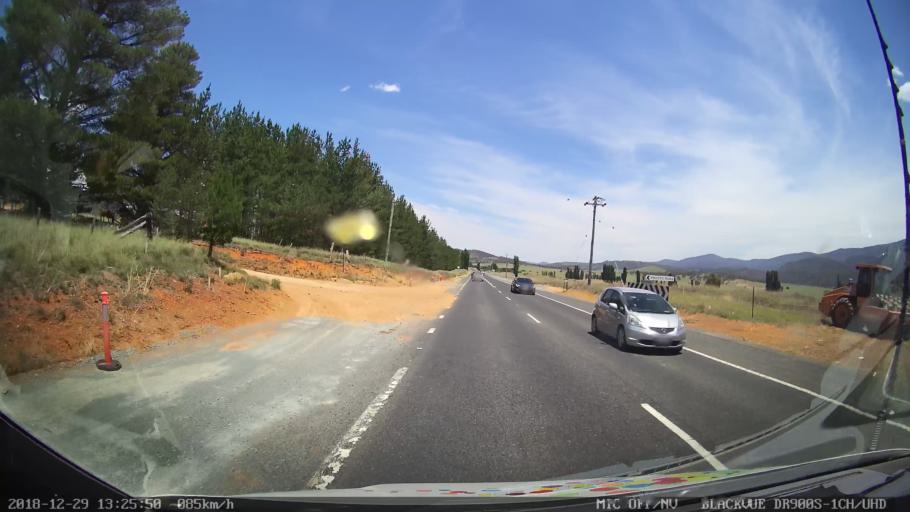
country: AU
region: New South Wales
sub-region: Cooma-Monaro
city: Cooma
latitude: -35.8477
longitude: 149.1604
